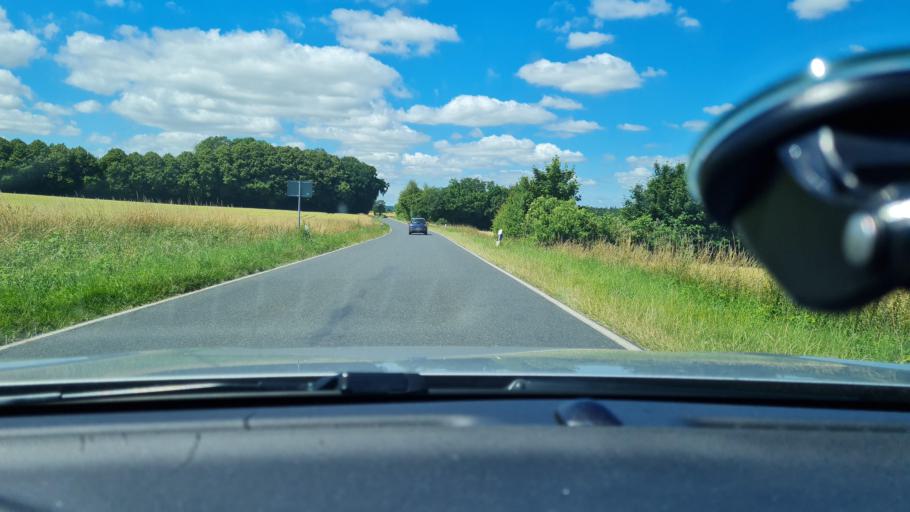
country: DE
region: Schleswig-Holstein
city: Thumby
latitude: 54.5847
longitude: 9.9010
